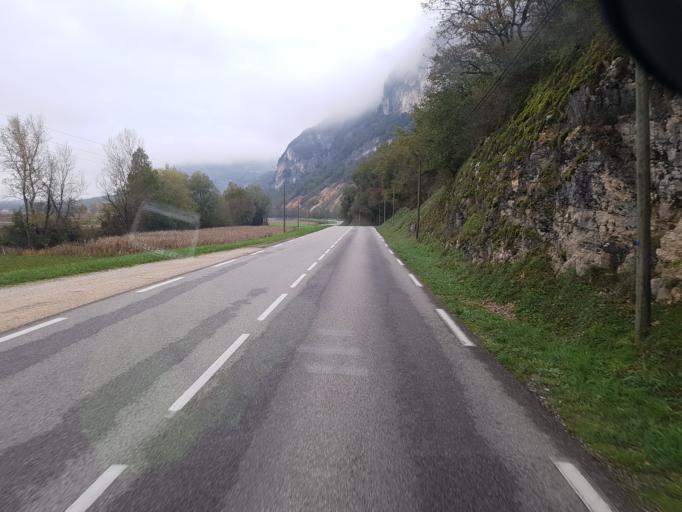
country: FR
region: Rhone-Alpes
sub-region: Departement de la Savoie
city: Yenne
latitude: 45.6926
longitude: 5.7141
